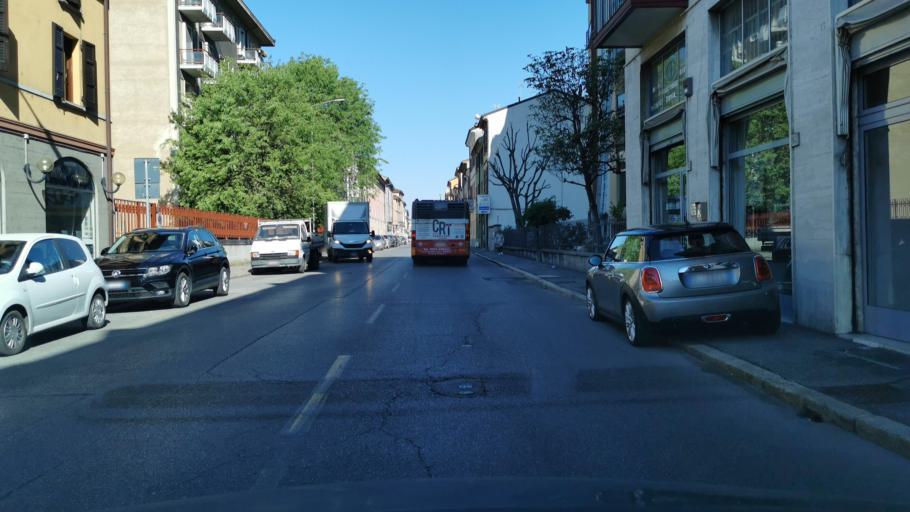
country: IT
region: Lombardy
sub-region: Provincia di Cremona
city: Cremona
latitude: 45.1301
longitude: 10.0193
